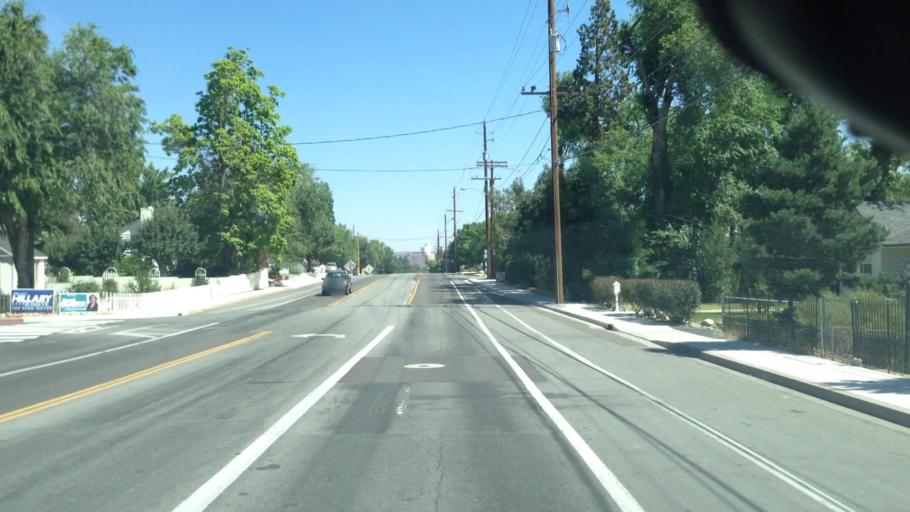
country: US
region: Nevada
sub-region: Washoe County
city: Reno
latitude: 39.5015
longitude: -119.8126
